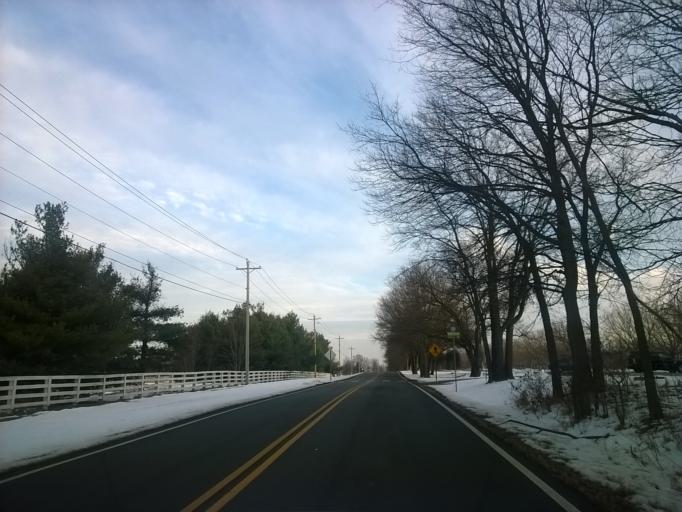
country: US
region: Indiana
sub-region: Hamilton County
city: Fishers
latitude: 39.9677
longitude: -86.0516
